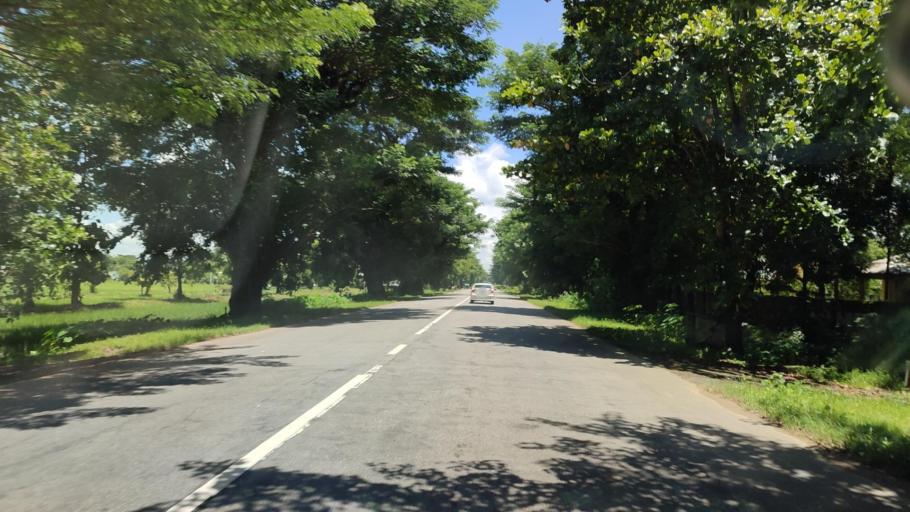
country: MM
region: Bago
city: Pyu
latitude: 18.2414
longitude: 96.5436
